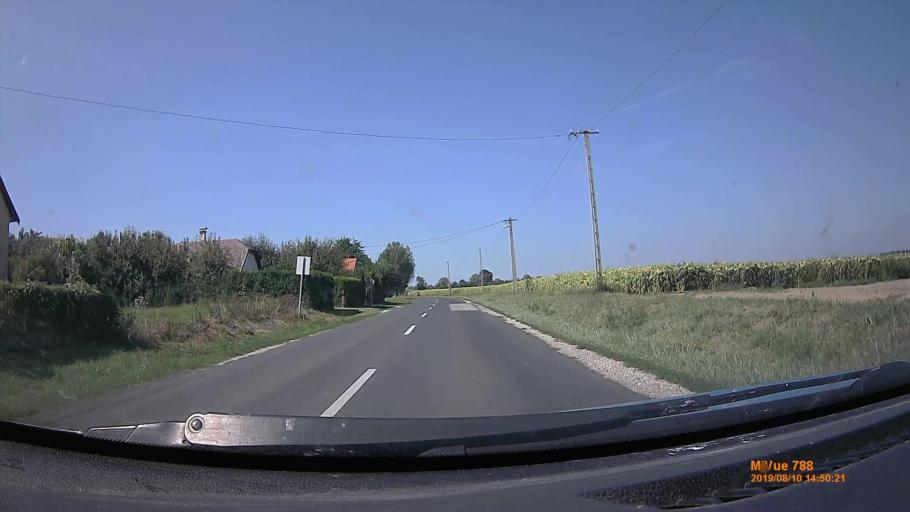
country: HU
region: Somogy
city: Somogyvar
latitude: 46.6059
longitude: 17.6434
